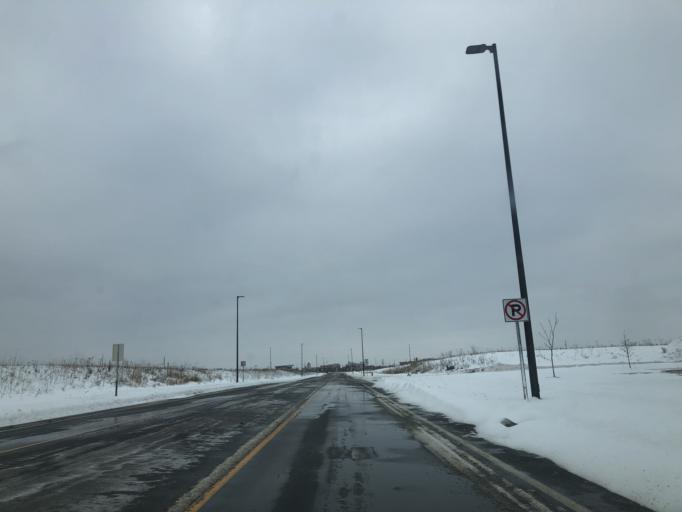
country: US
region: Minnesota
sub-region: Hennepin County
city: Osseo
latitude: 45.0920
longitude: -93.4159
